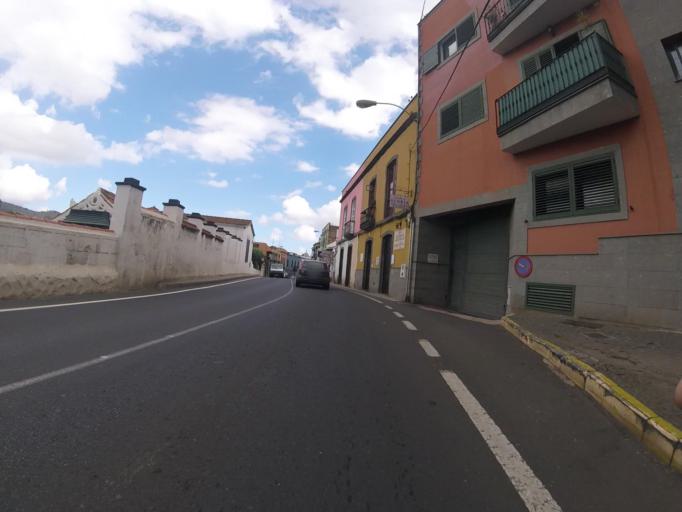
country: ES
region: Canary Islands
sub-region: Provincia de Las Palmas
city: Santa Brigida
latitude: 28.0321
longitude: -15.4992
